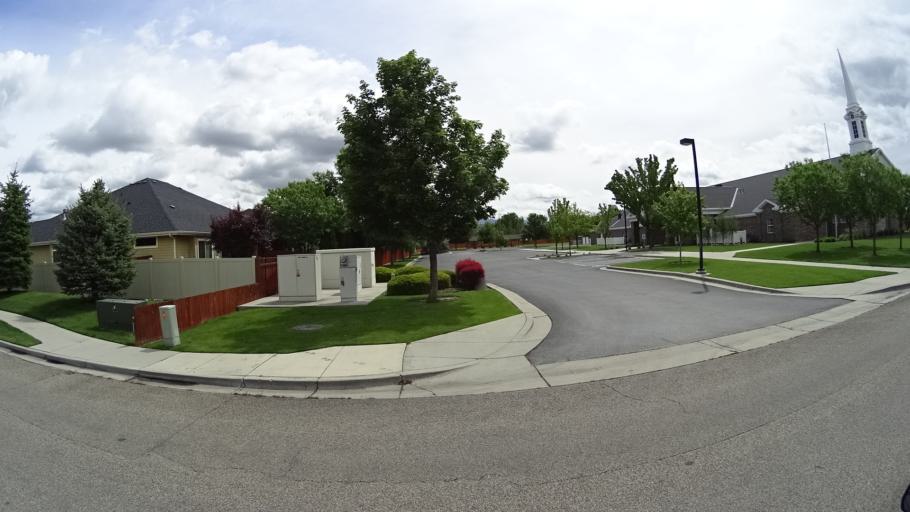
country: US
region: Idaho
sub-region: Ada County
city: Eagle
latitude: 43.6820
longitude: -116.3015
